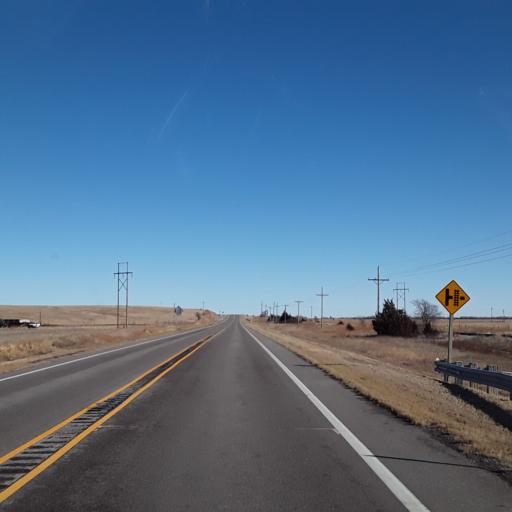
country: US
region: Kansas
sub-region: Pawnee County
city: Larned
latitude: 38.0854
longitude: -99.2290
